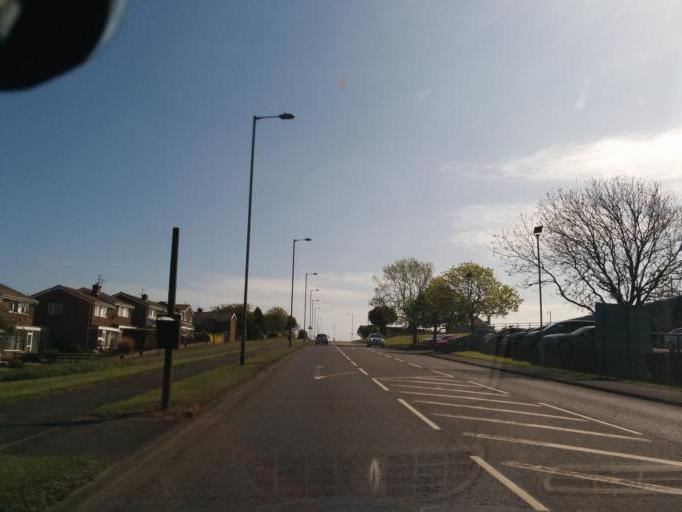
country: GB
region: England
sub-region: Northumberland
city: Newbiggin-by-the-Sea
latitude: 55.1709
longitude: -1.5479
